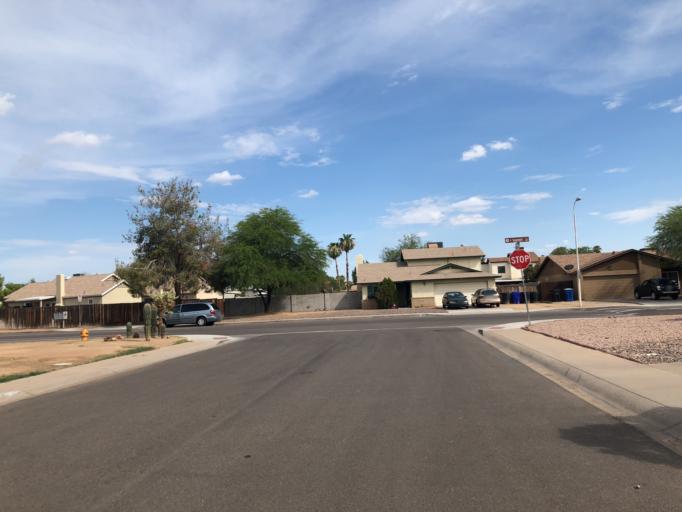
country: US
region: Arizona
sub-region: Maricopa County
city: San Carlos
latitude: 33.3553
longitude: -111.8715
